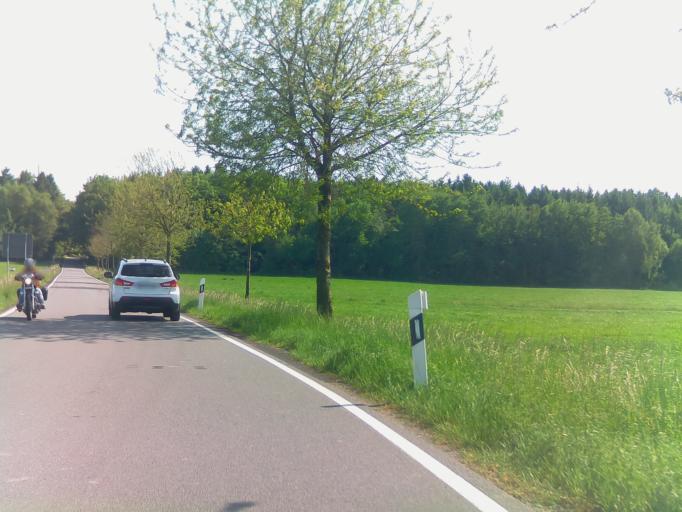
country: DE
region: Hesse
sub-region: Regierungsbezirk Darmstadt
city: Lutzelbach
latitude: 49.7130
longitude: 9.0864
